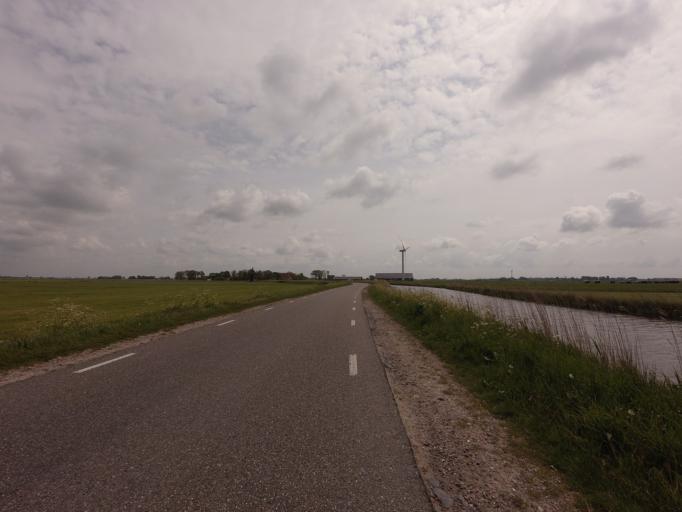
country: NL
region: Friesland
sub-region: Sudwest Fryslan
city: Bolsward
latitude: 53.1010
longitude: 5.5155
